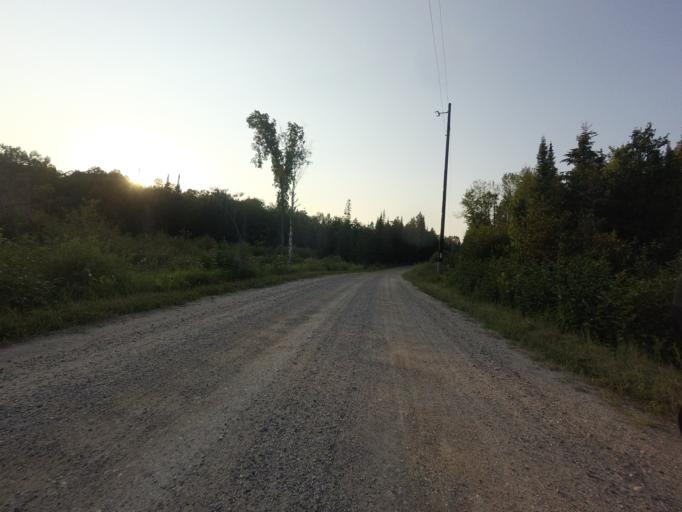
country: CA
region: Ontario
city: Renfrew
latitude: 45.0616
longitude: -76.7545
